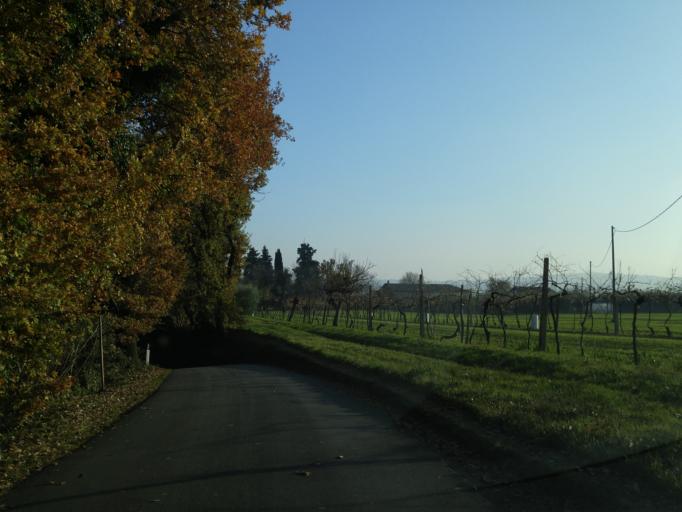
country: IT
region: The Marches
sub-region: Provincia di Pesaro e Urbino
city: Cuccurano
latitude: 43.7775
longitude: 12.9611
